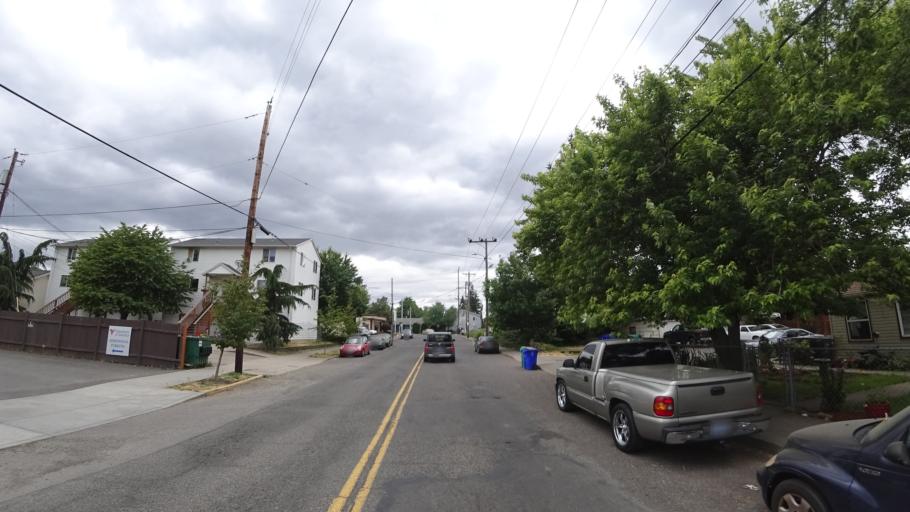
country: US
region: Oregon
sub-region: Multnomah County
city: Lents
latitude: 45.5031
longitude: -122.5237
